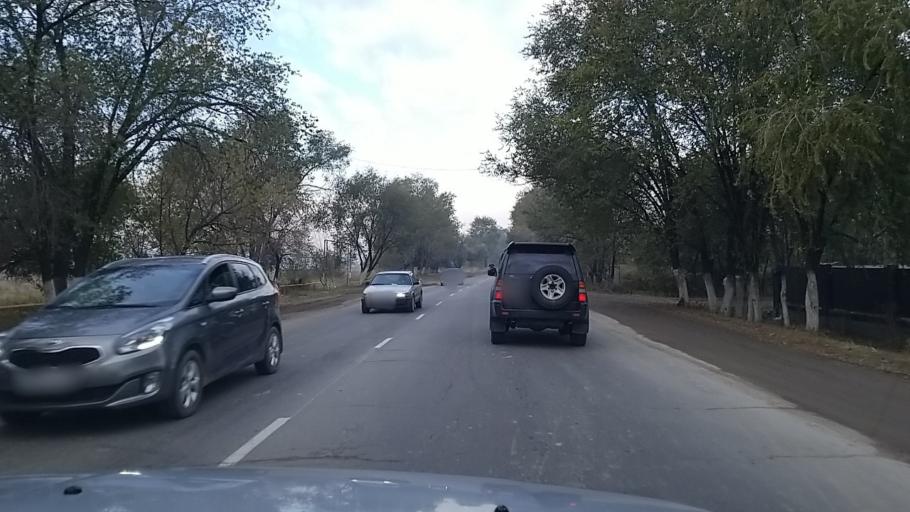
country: KZ
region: Almaty Oblysy
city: Burunday
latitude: 43.3592
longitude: 76.7545
